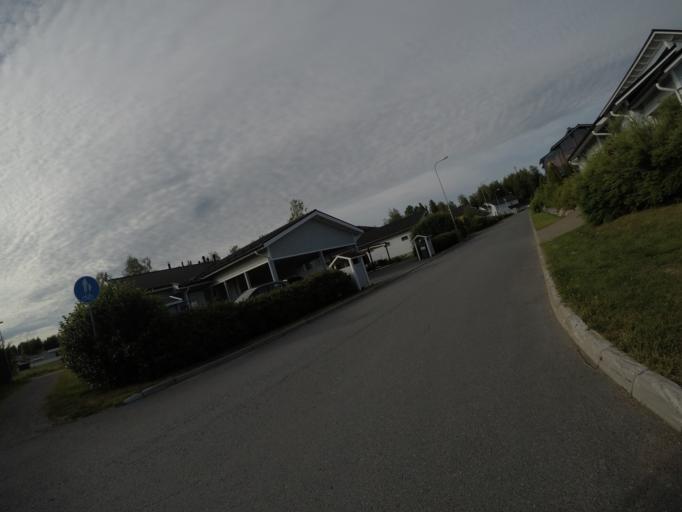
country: FI
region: Haeme
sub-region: Haemeenlinna
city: Parola
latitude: 60.9764
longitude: 24.3838
